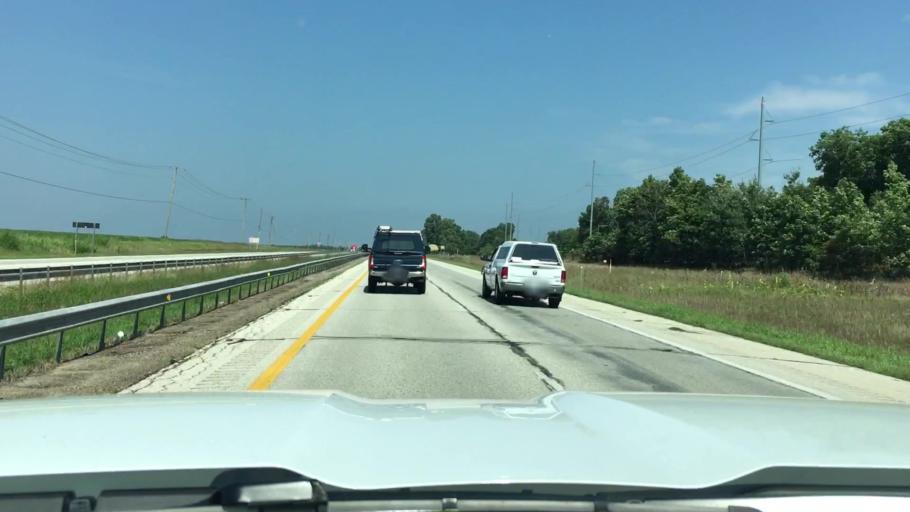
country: US
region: Michigan
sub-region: Kalamazoo County
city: Schoolcraft
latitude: 42.0649
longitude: -85.6361
